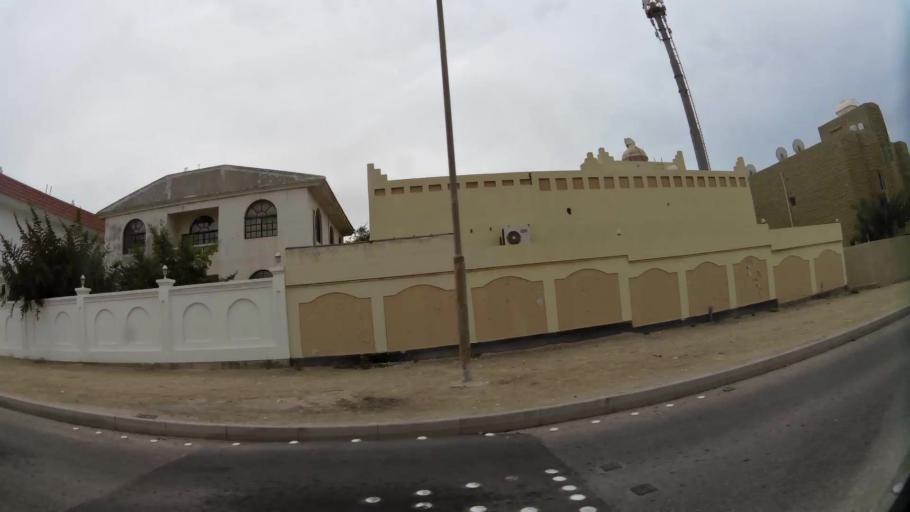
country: BH
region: Central Governorate
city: Madinat Hamad
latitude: 26.1077
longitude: 50.5010
